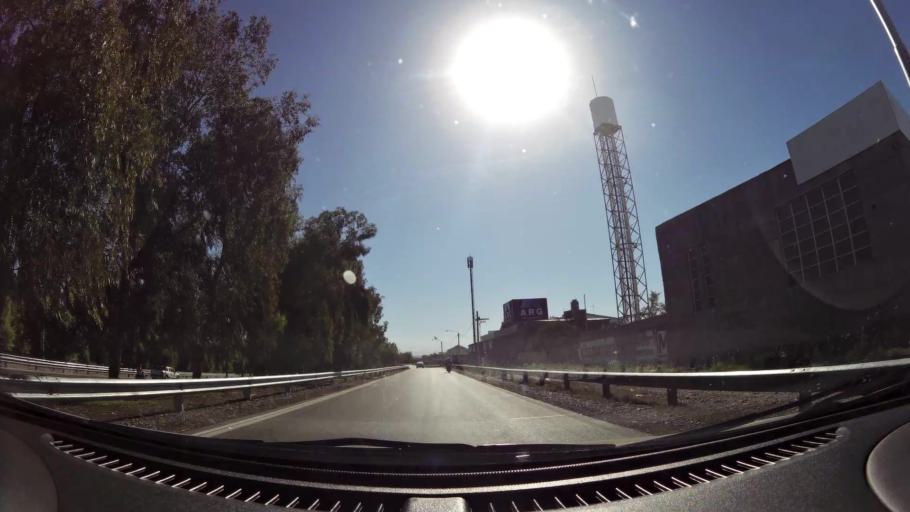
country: AR
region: San Juan
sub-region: Departamento de Santa Lucia
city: Santa Lucia
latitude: -31.5162
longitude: -68.5140
